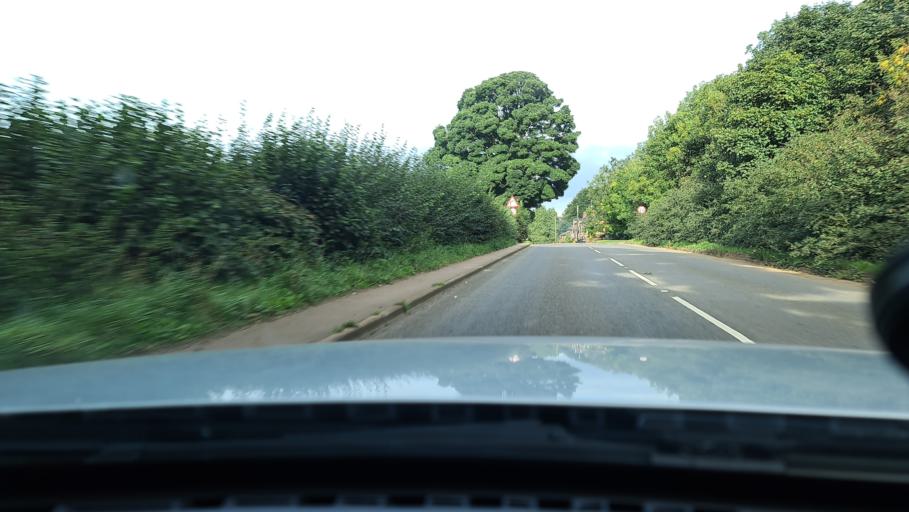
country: GB
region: England
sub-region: Oxfordshire
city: Hanwell
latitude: 52.0712
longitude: -1.3714
